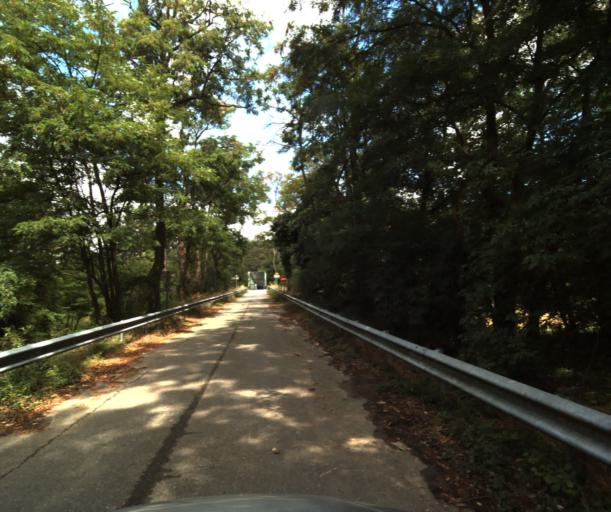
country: FR
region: Midi-Pyrenees
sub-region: Departement de la Haute-Garonne
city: Lacroix-Falgarde
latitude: 43.4961
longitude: 1.4077
